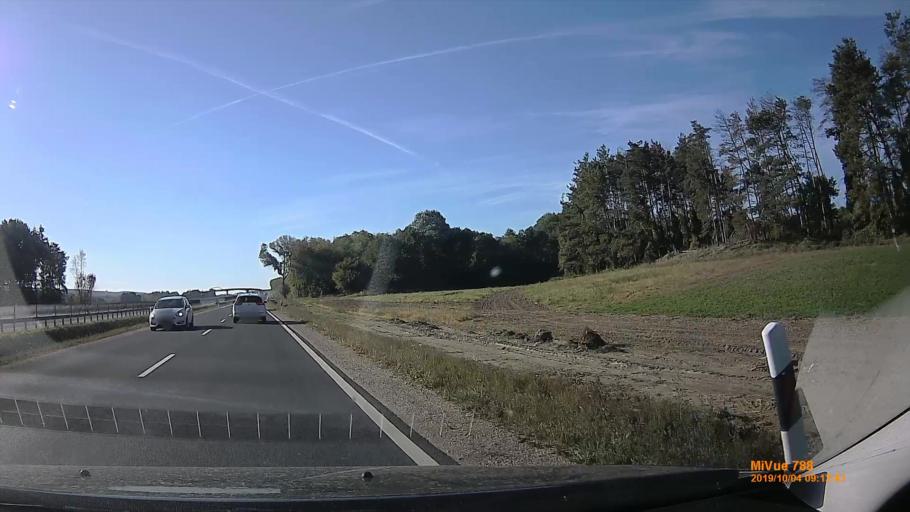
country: HU
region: Somogy
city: Karad
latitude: 46.6451
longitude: 17.7868
